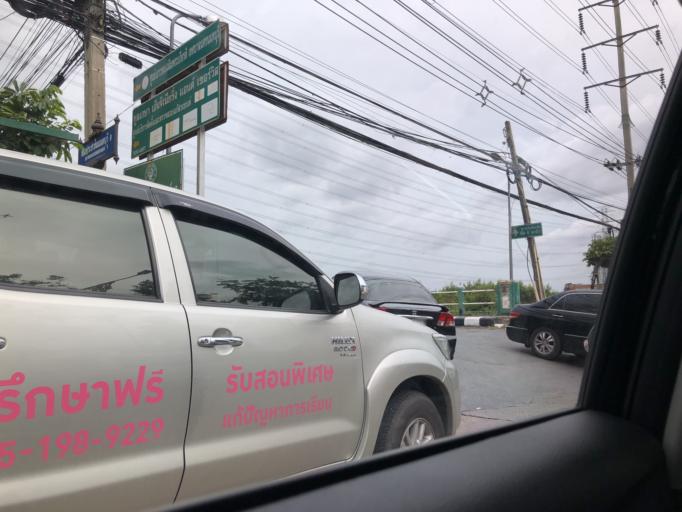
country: TH
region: Bangkok
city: Lak Si
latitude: 13.8755
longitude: 100.5496
